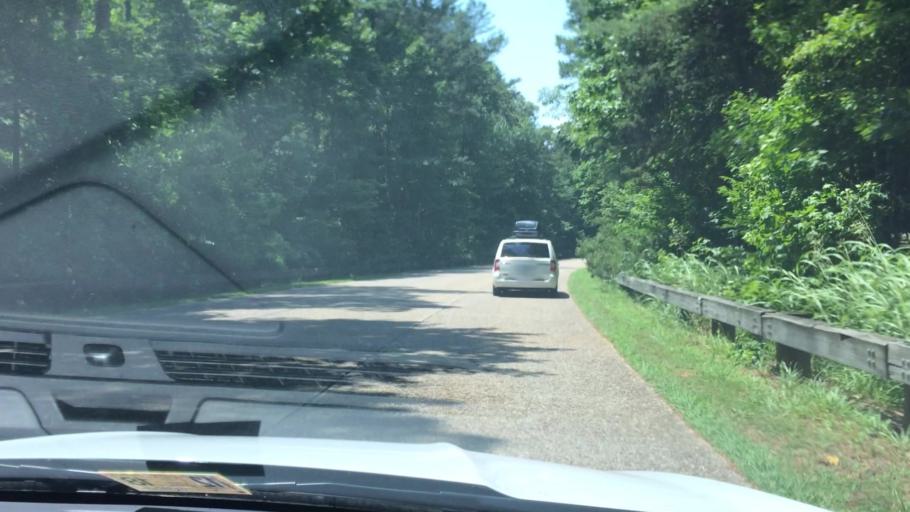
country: US
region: Virginia
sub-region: York County
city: Yorktown
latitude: 37.2288
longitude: -76.5158
